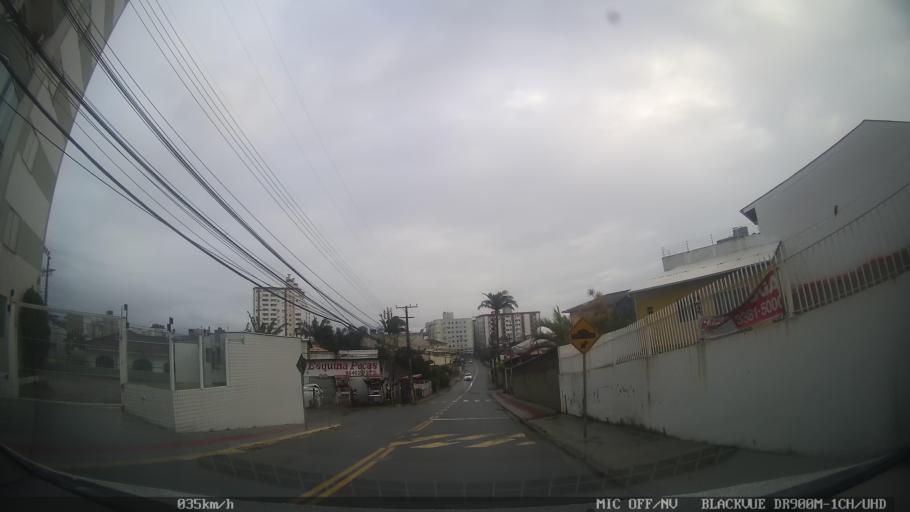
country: BR
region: Santa Catarina
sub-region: Sao Jose
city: Campinas
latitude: -27.5782
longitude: -48.6091
